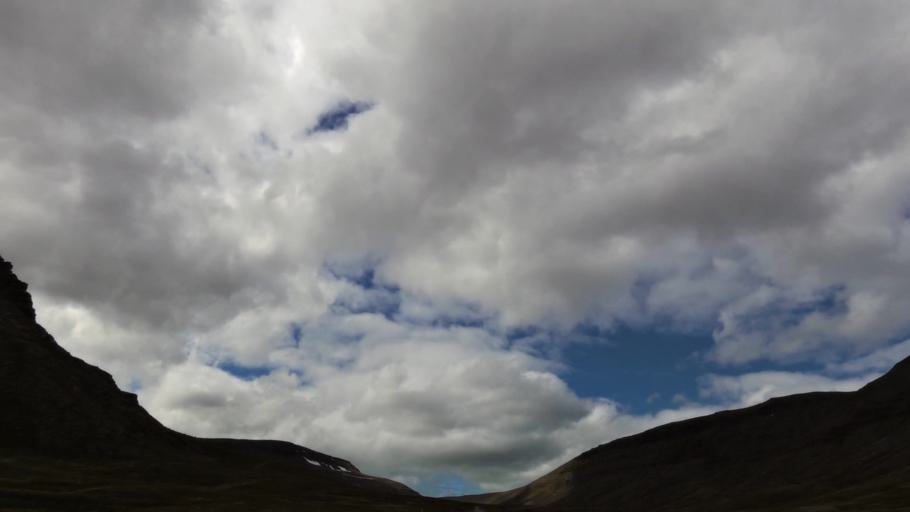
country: IS
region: Westfjords
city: Isafjoerdur
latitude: 66.1581
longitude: -23.2931
